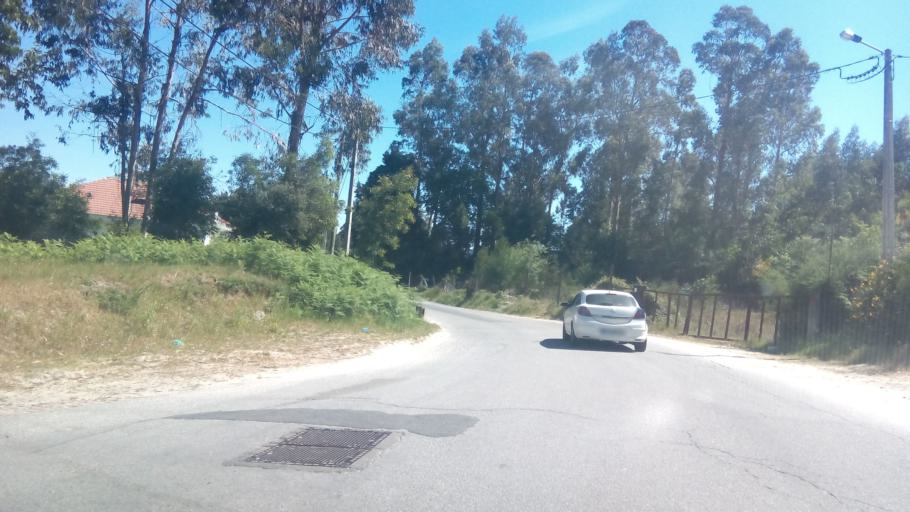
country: PT
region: Porto
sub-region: Paredes
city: Baltar
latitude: 41.1882
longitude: -8.3603
